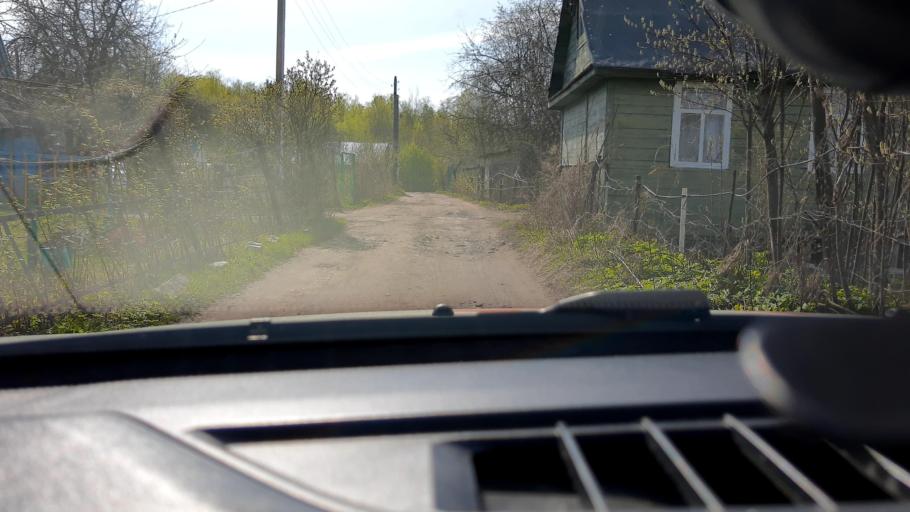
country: RU
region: Nizjnij Novgorod
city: Gorbatovka
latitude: 56.2777
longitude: 43.7877
